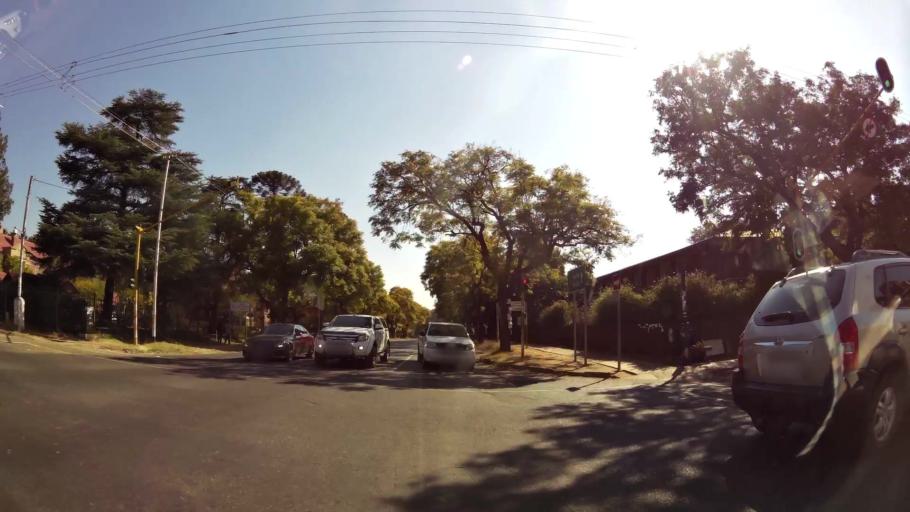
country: ZA
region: Gauteng
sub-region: City of Tshwane Metropolitan Municipality
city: Pretoria
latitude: -25.7561
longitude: 28.2012
